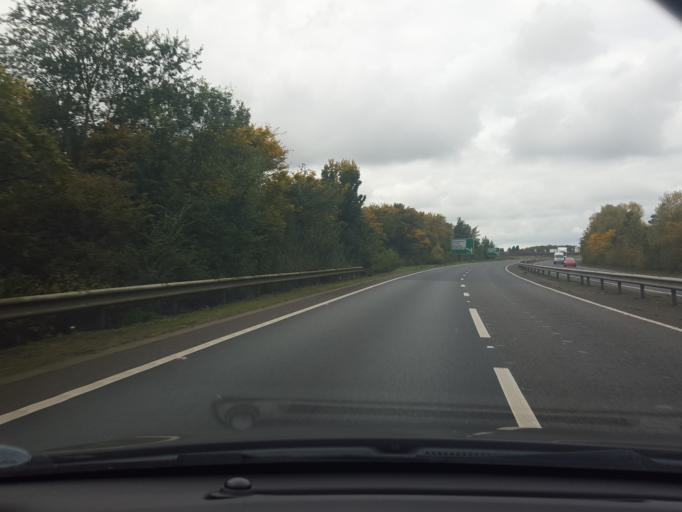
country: GB
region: England
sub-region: Suffolk
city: Stowmarket
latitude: 52.1983
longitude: 0.9893
